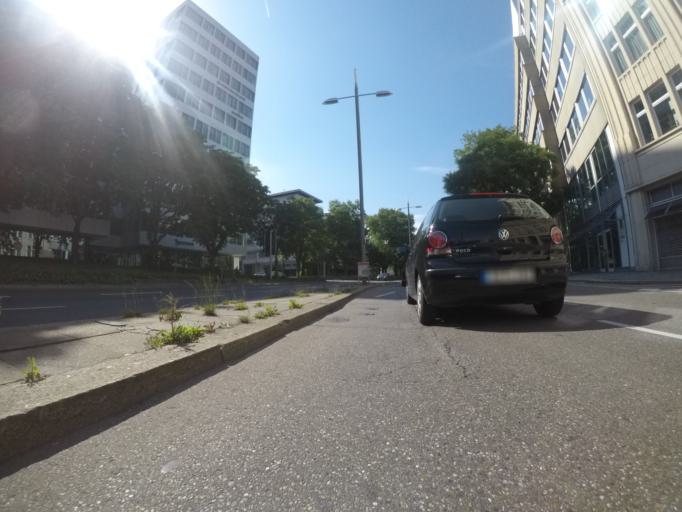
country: DE
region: Baden-Wuerttemberg
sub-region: Regierungsbezirk Stuttgart
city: Stuttgart
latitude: 48.7724
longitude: 9.1709
